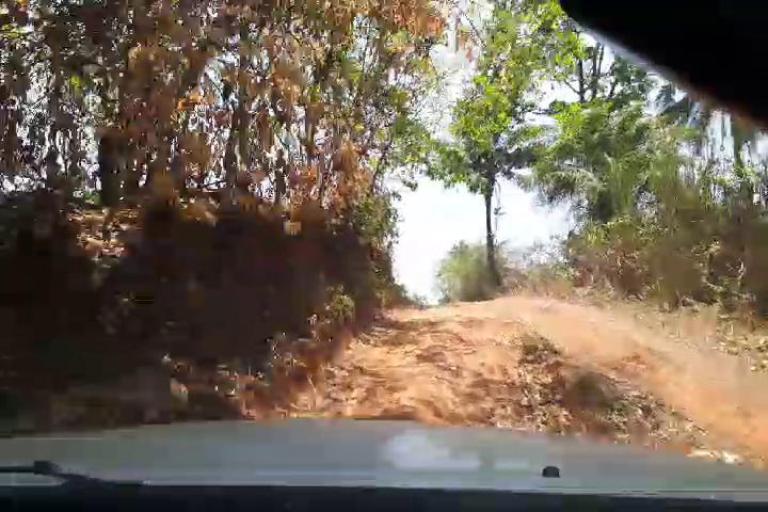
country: SL
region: Northern Province
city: Alikalia
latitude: 9.0738
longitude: -11.4781
